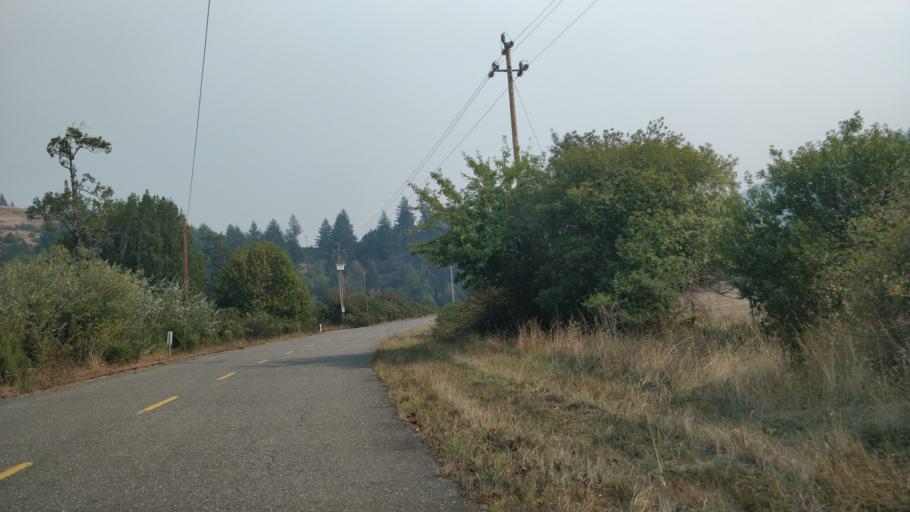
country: US
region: California
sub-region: Humboldt County
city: Rio Dell
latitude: 40.2789
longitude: -124.2451
